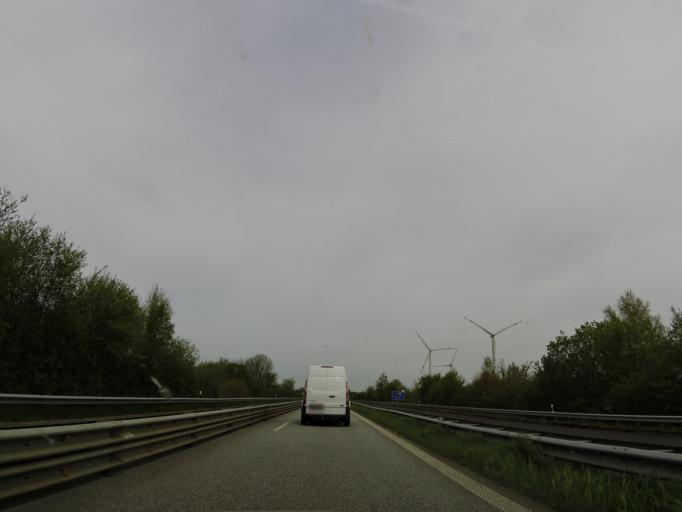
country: DE
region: Schleswig-Holstein
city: Tensbuttel-Rost
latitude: 54.1287
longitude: 9.2546
